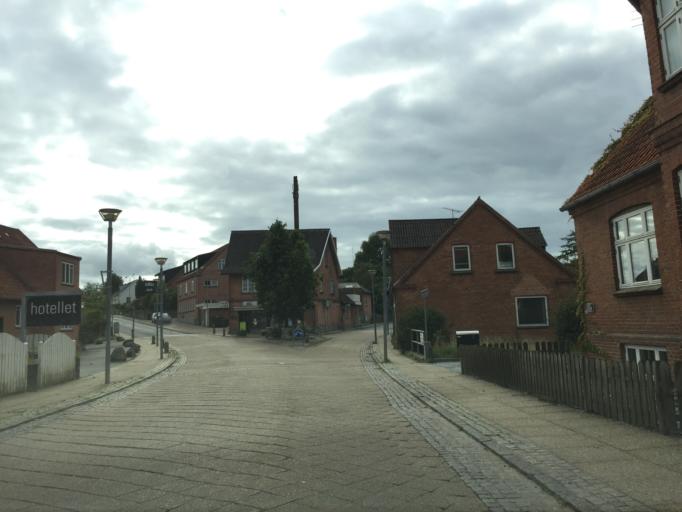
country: DK
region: Central Jutland
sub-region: Favrskov Kommune
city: Hammel
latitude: 56.2303
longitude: 9.7390
